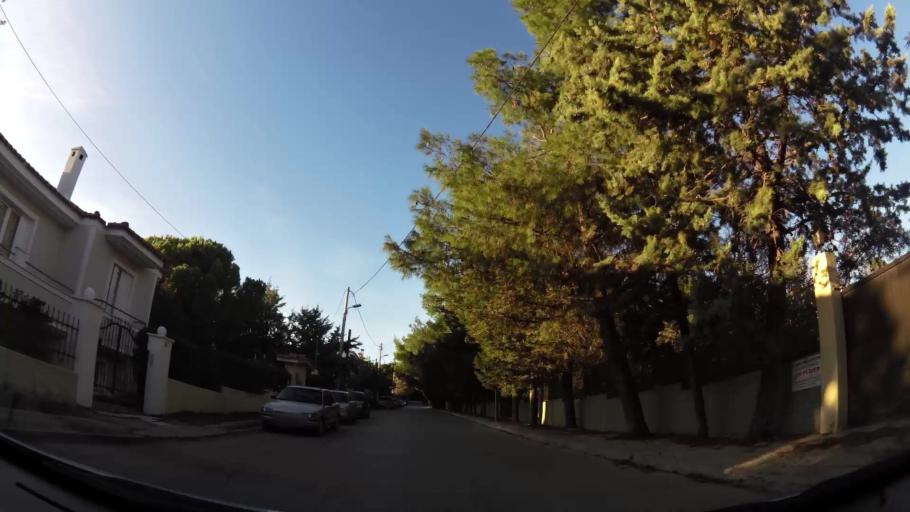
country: GR
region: Attica
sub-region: Nomarchia Anatolikis Attikis
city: Kryoneri
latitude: 38.1367
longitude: 23.8239
